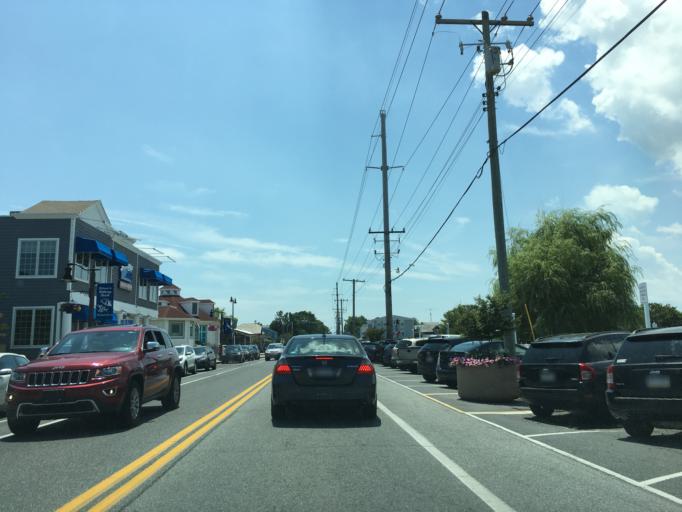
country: US
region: Delaware
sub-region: Sussex County
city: Bethany Beach
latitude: 38.5393
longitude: -75.0573
